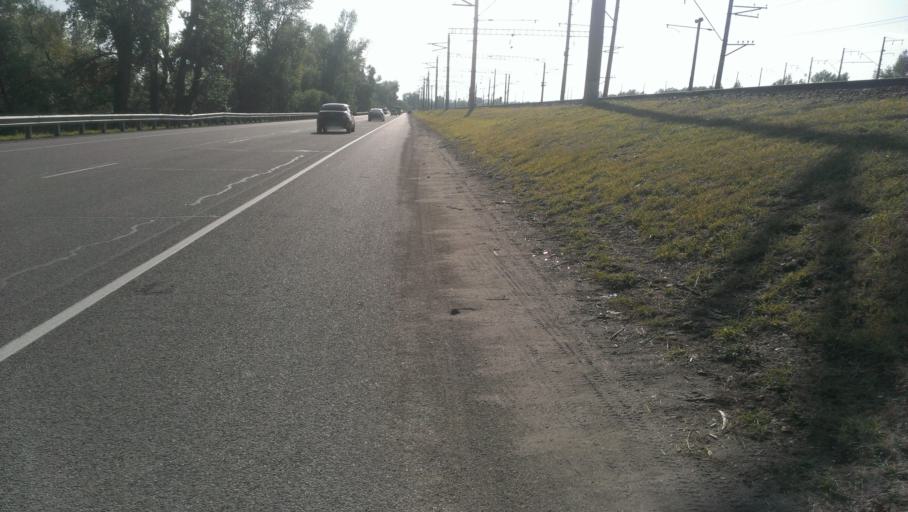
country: RU
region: Altai Krai
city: Novoaltaysk
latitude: 53.3685
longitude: 83.8565
